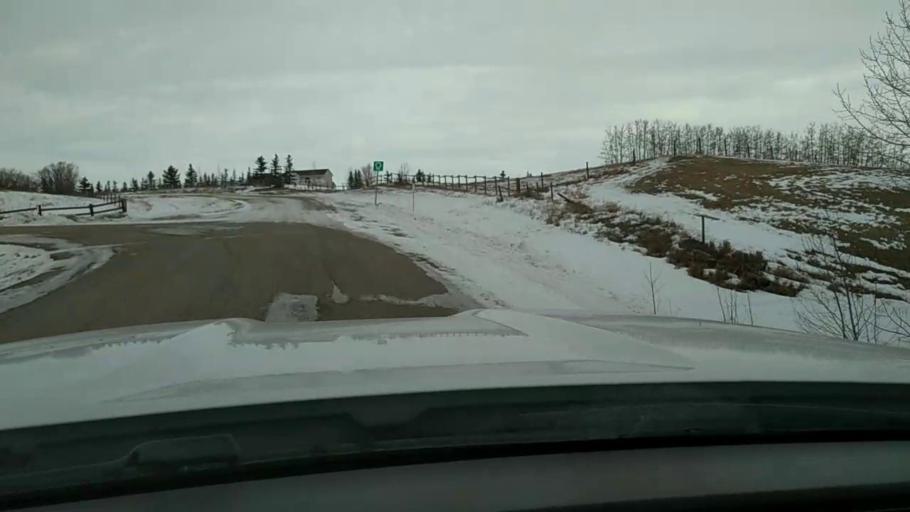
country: CA
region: Alberta
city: Cochrane
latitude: 51.1998
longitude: -114.2864
